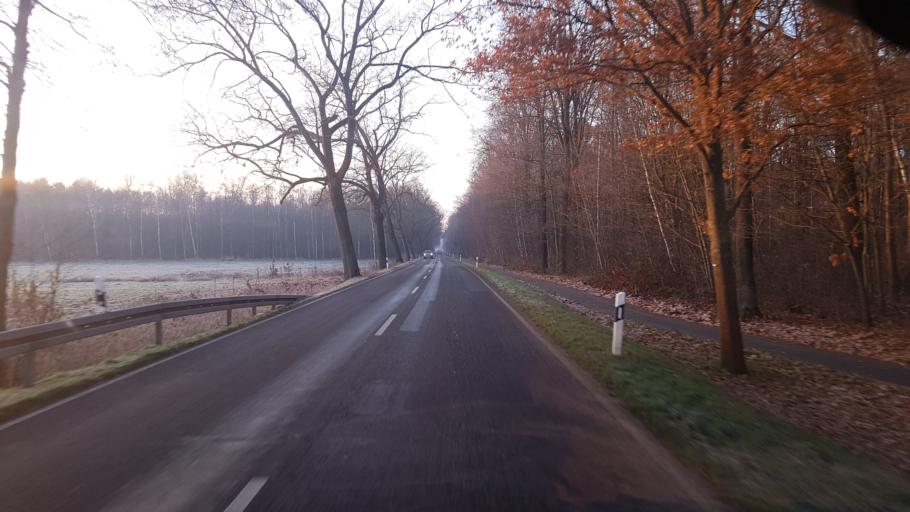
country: DE
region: Brandenburg
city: Tettau
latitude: 51.4482
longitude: 13.7364
